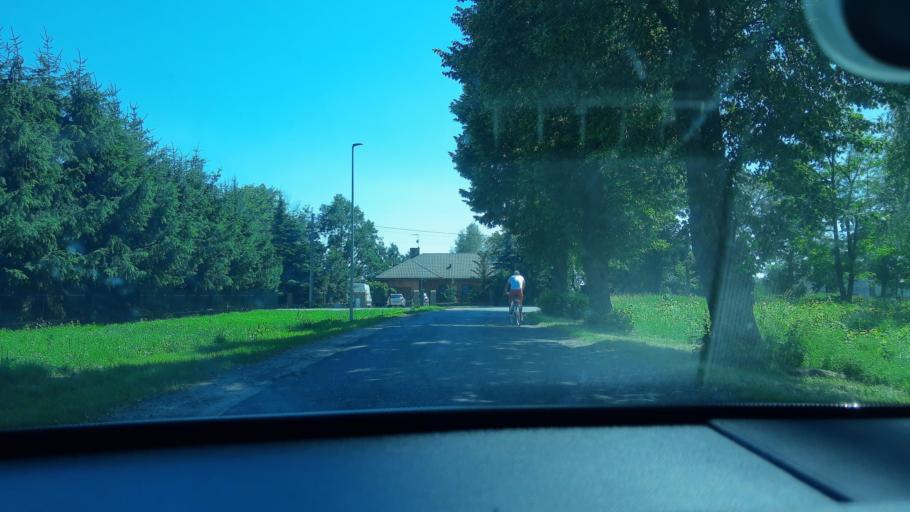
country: PL
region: Lodz Voivodeship
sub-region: Powiat zdunskowolski
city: Zdunska Wola
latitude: 51.6177
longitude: 18.9710
